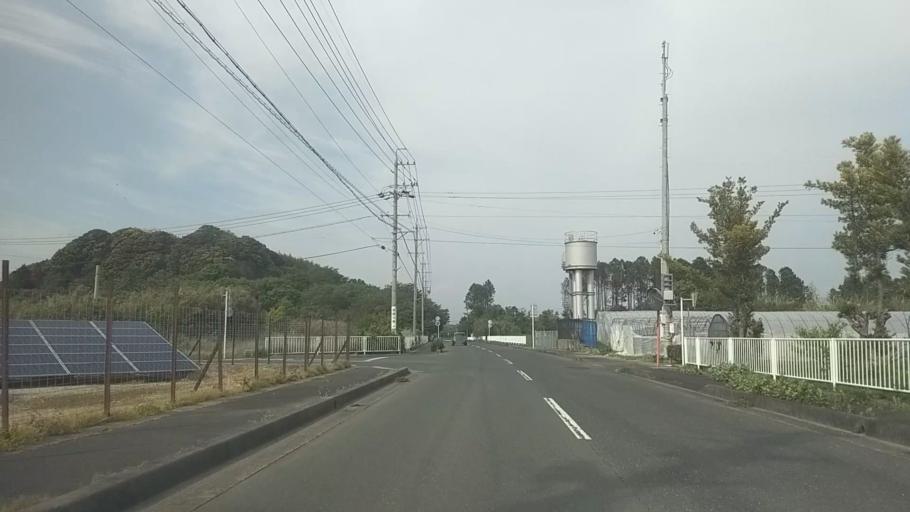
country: JP
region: Shizuoka
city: Kosai-shi
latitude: 34.7252
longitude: 137.6027
